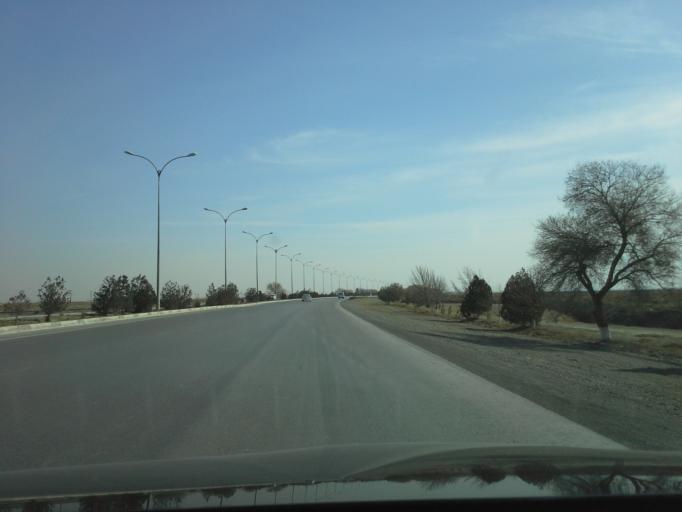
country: TM
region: Ahal
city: Abadan
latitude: 38.1346
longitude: 58.0137
